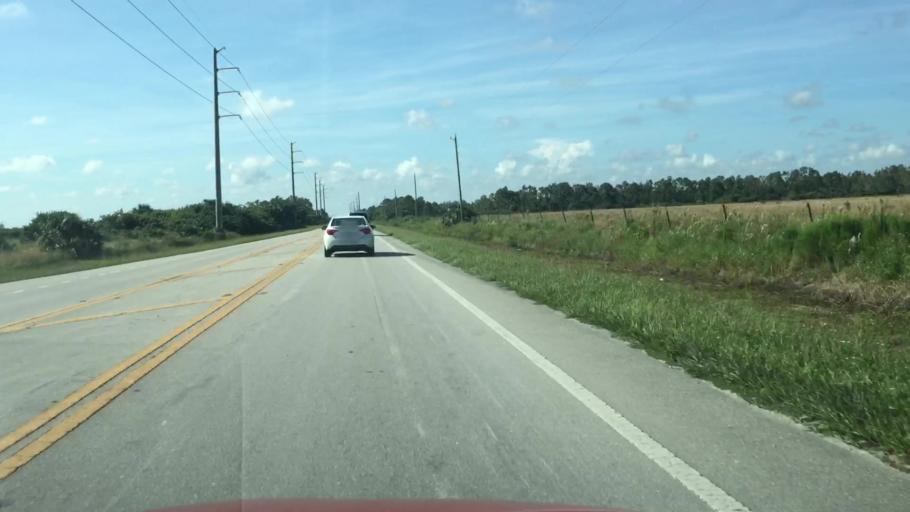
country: US
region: Florida
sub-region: Collier County
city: Orangetree
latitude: 26.3259
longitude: -81.5950
